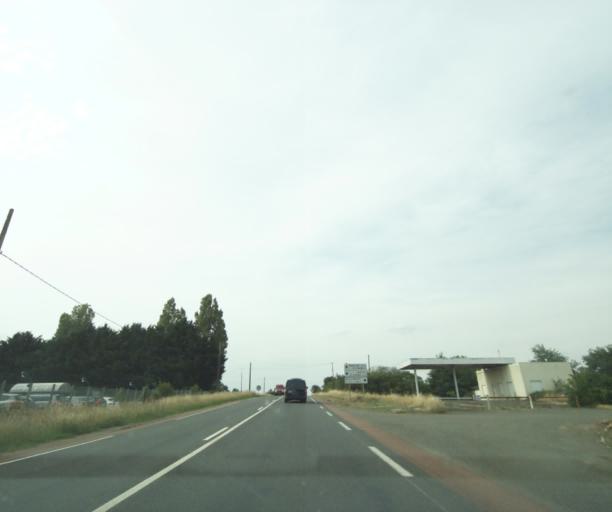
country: FR
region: Pays de la Loire
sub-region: Departement de la Sarthe
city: Luceau
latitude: 47.7194
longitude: 0.4004
